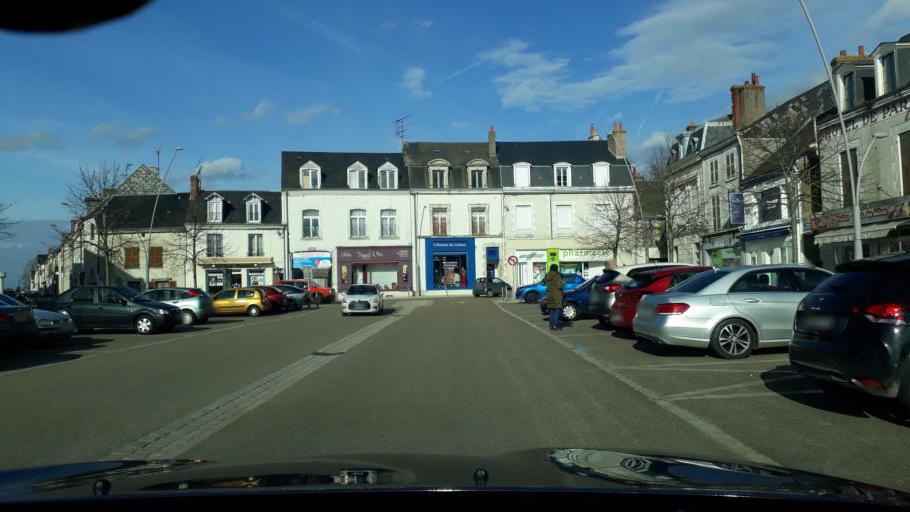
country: FR
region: Centre
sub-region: Departement du Loiret
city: Neuville-aux-Bois
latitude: 48.0699
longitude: 2.0536
